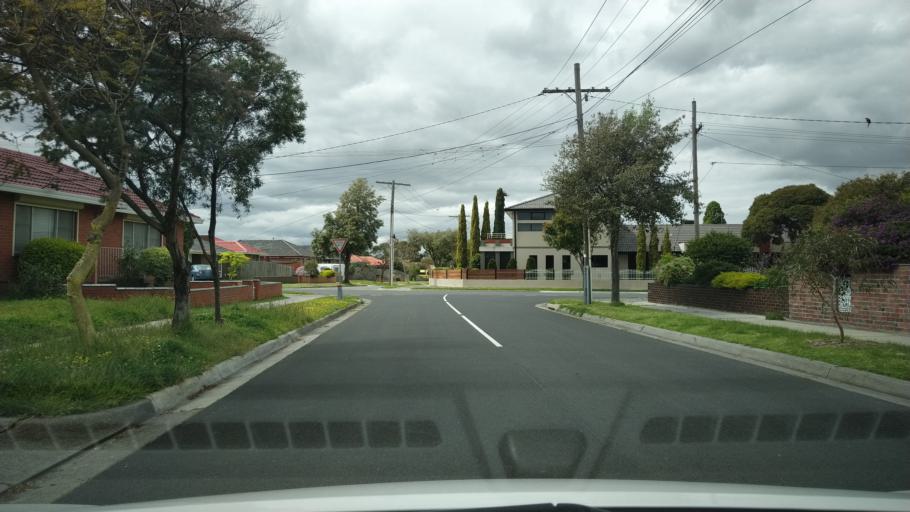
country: AU
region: Victoria
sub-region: Greater Dandenong
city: Noble Park
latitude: -37.9758
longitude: 145.1806
